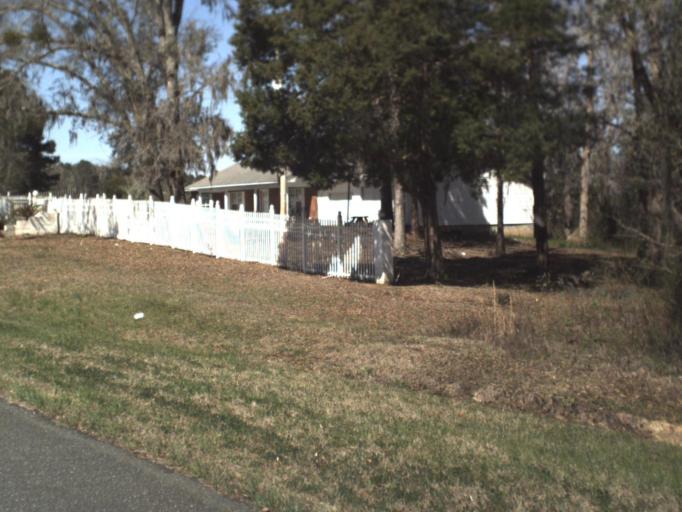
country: US
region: Florida
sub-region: Jackson County
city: Marianna
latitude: 30.7855
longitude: -85.3433
